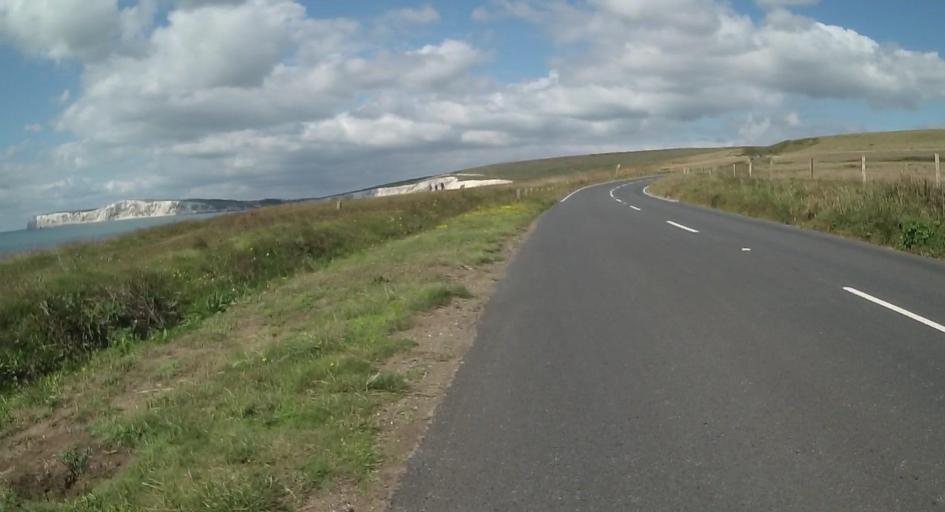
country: GB
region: England
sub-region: Isle of Wight
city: Freshwater
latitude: 50.6557
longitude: -1.4659
